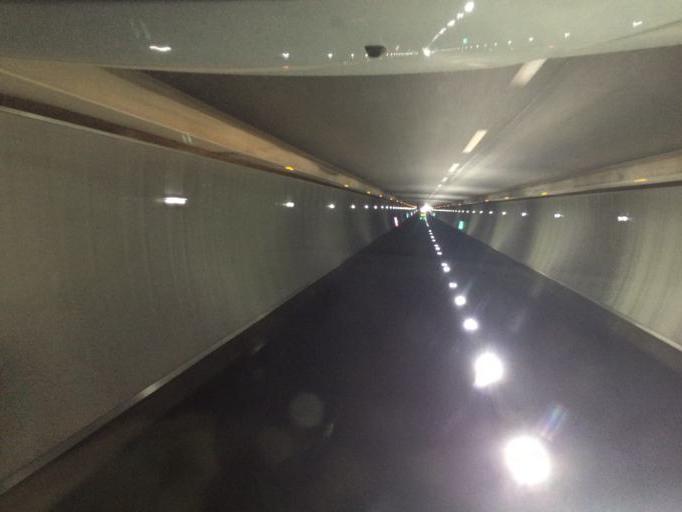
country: IT
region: Umbria
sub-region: Provincia di Perugia
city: Massa Martana
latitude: 42.7463
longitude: 12.4712
